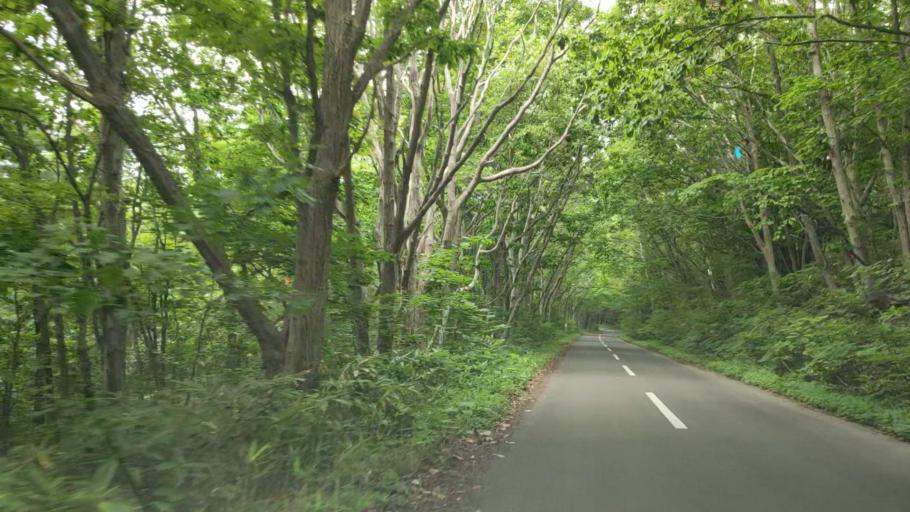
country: JP
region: Hokkaido
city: Otaru
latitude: 43.1966
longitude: 140.9828
